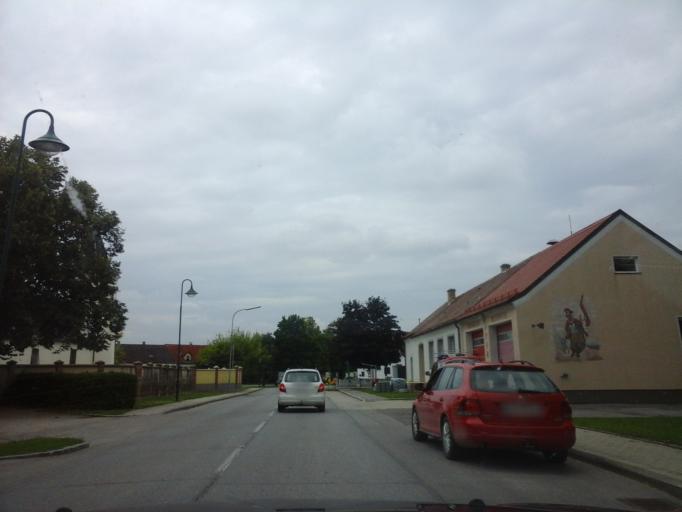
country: AT
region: Lower Austria
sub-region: Politischer Bezirk Ganserndorf
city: Eckartsau
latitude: 48.1645
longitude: 16.7837
